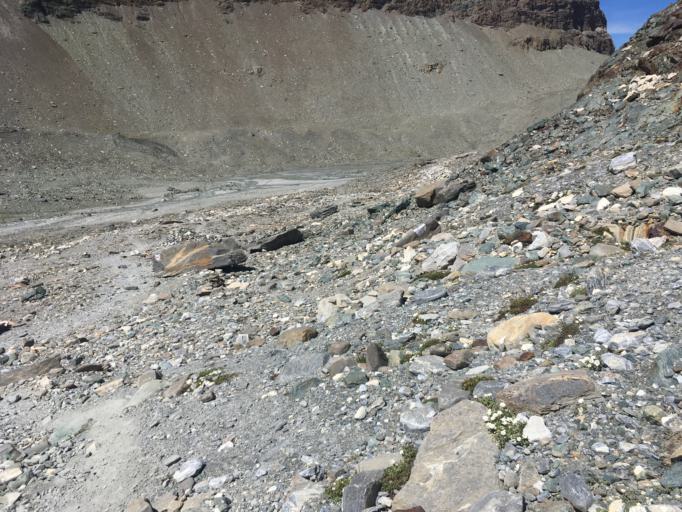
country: CH
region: Valais
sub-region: Visp District
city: Zermatt
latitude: 45.9807
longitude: 7.6911
